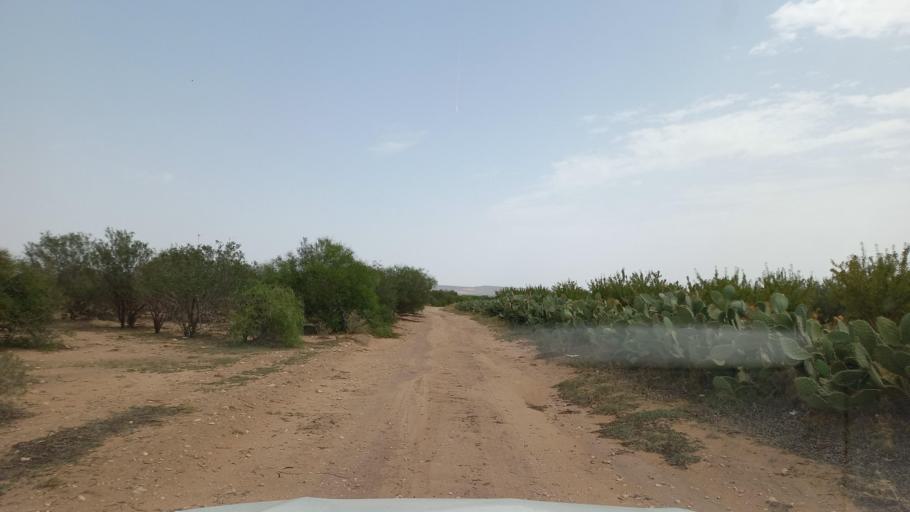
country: TN
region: Al Qasrayn
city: Kasserine
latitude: 35.2930
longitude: 9.0119
